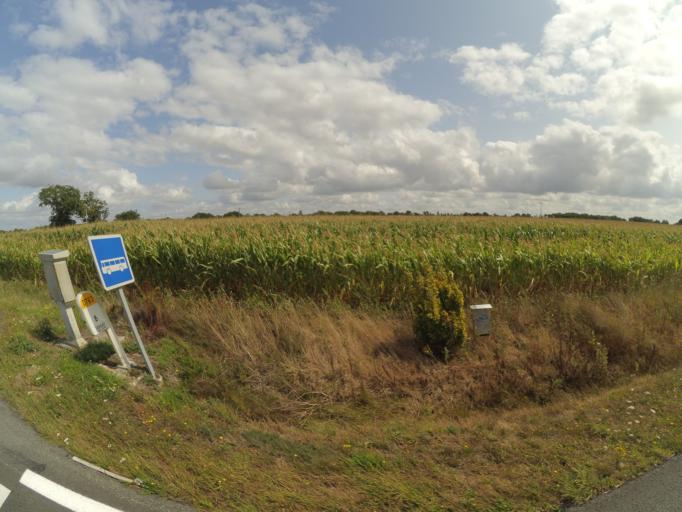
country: FR
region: Pays de la Loire
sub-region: Departement de la Vendee
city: La Bernardiere
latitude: 47.0167
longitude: -1.2749
